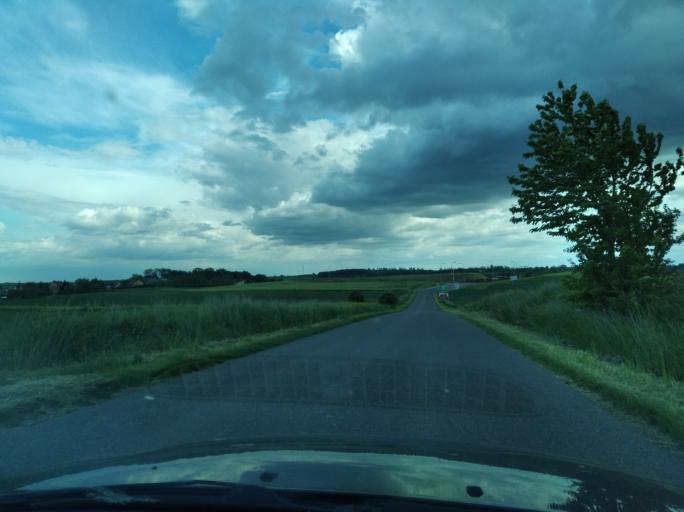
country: PL
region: Subcarpathian Voivodeship
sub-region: Powiat jaroslawski
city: Pawlosiow
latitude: 49.9499
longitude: 22.6667
